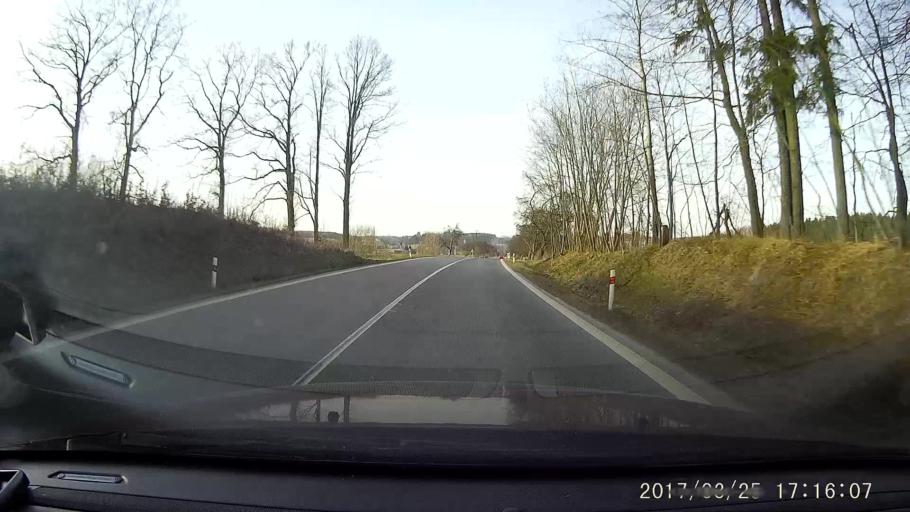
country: CZ
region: Liberecky
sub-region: Okres Liberec
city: Frydlant
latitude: 50.9537
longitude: 15.0955
